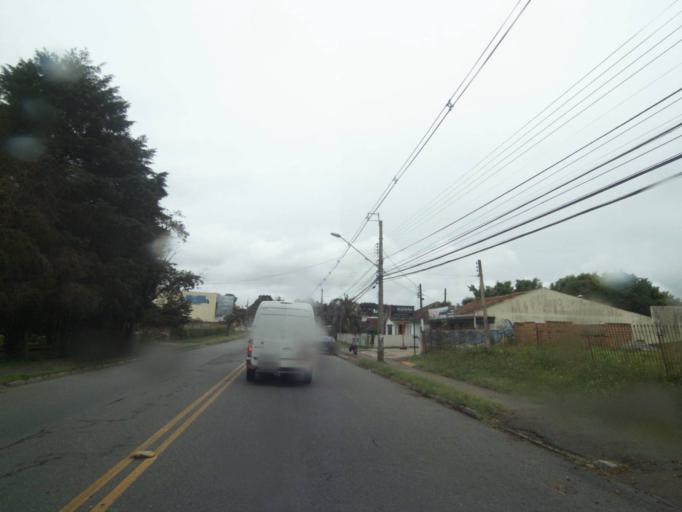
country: BR
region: Parana
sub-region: Curitiba
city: Curitiba
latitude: -25.4484
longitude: -49.3506
